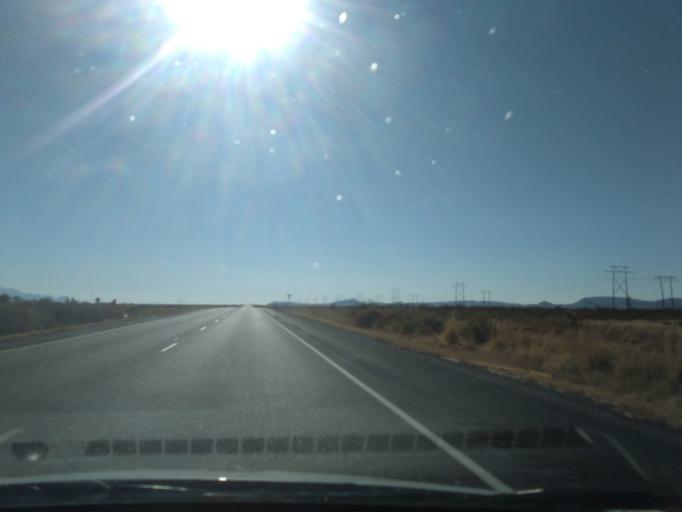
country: US
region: New Mexico
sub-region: Luna County
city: Deming
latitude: 32.4862
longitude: -107.5237
